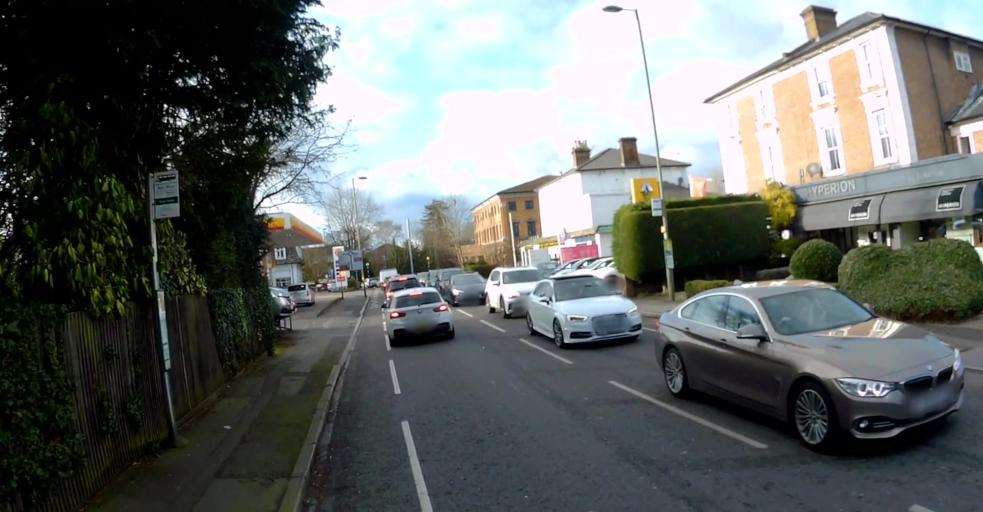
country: GB
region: England
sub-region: Surrey
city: Weybridge
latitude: 51.3715
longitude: -0.4495
